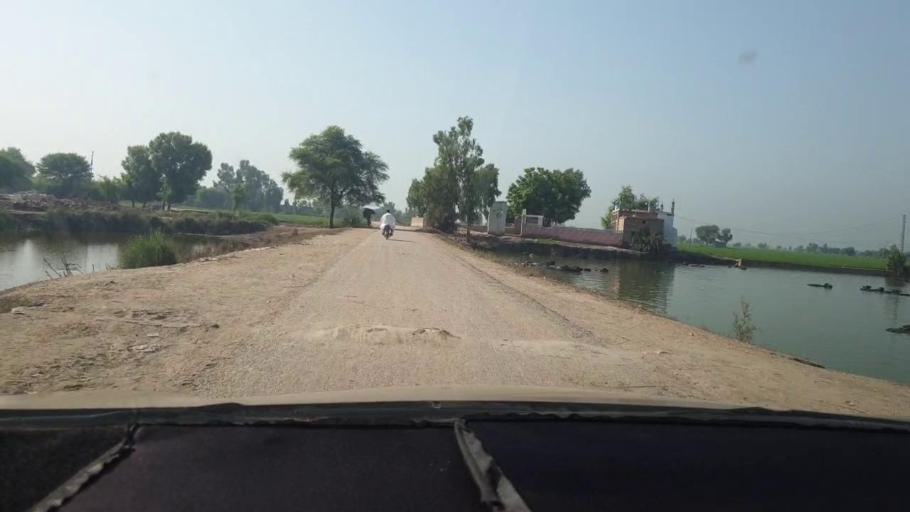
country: PK
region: Sindh
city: Kambar
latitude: 27.6013
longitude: 68.0933
